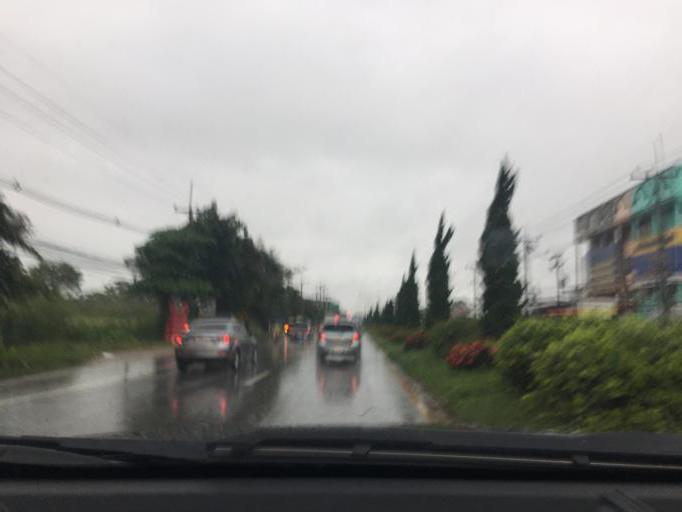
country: TH
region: Chiang Rai
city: Chiang Rai
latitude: 20.0074
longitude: 99.8679
